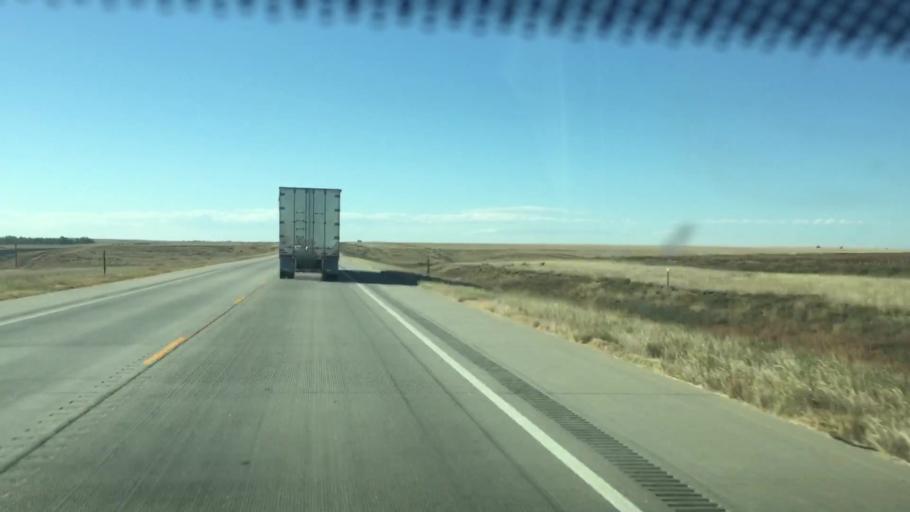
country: US
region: Colorado
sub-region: Kiowa County
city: Eads
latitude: 38.8009
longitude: -102.9576
